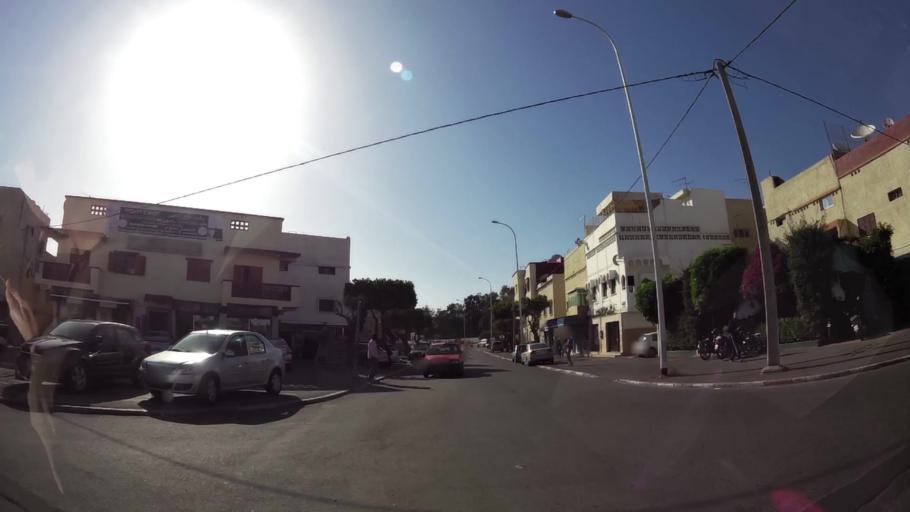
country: MA
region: Souss-Massa-Draa
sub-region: Agadir-Ida-ou-Tnan
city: Agadir
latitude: 30.4270
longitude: -9.5843
